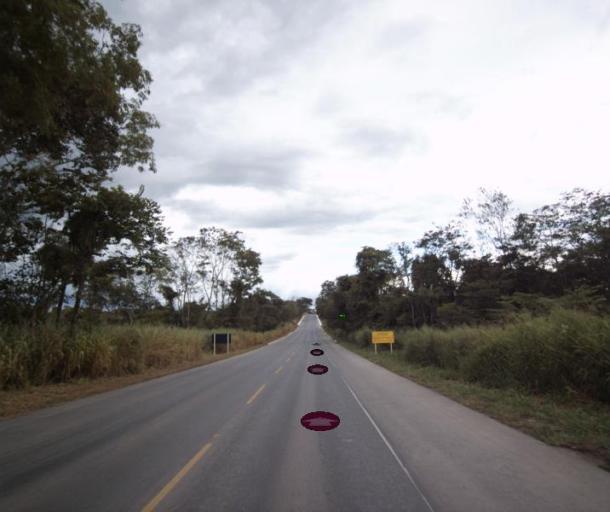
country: BR
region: Goias
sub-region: Itapaci
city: Itapaci
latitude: -14.9867
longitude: -49.4019
